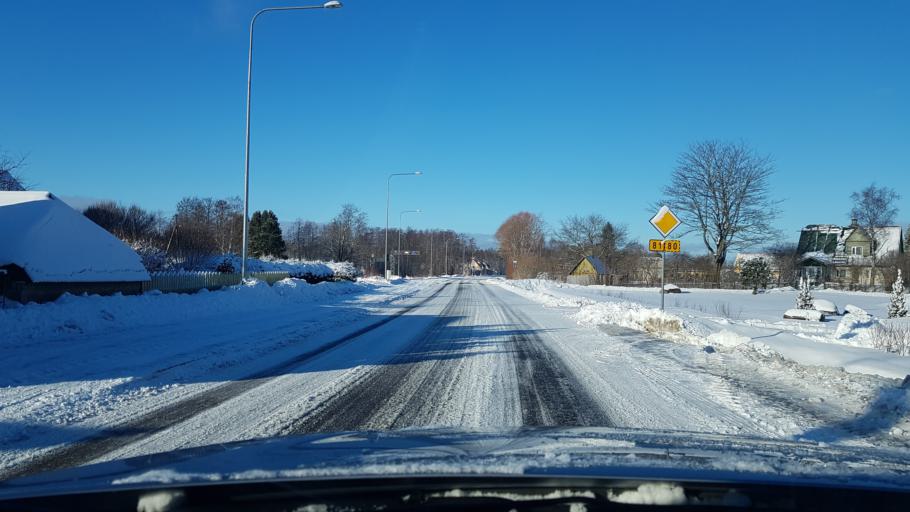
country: EE
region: Hiiumaa
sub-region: Kaerdla linn
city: Kardla
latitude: 58.9852
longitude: 22.7564
